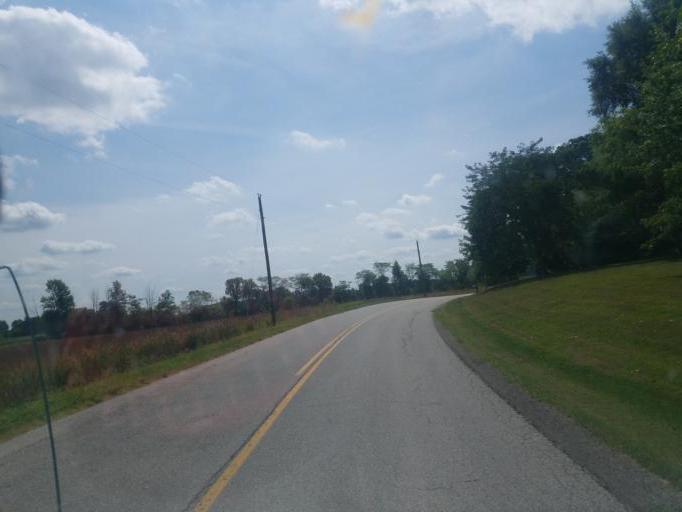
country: US
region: Ohio
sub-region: Union County
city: Marysville
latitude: 40.3088
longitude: -83.2926
